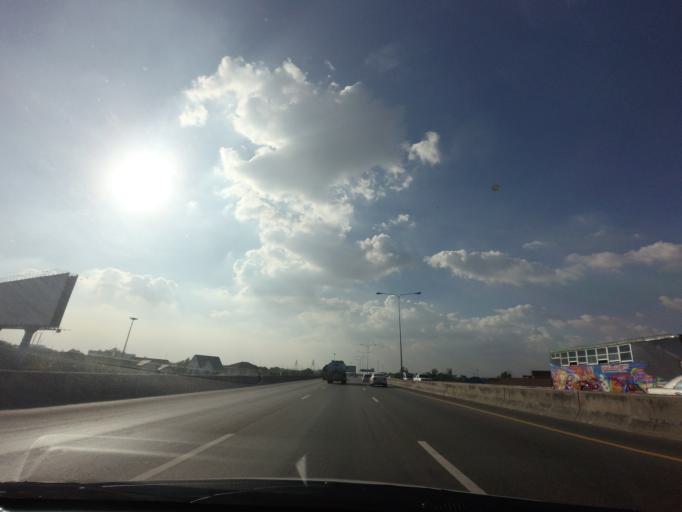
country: TH
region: Samut Prakan
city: Phra Samut Chedi
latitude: 13.6324
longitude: 100.5754
